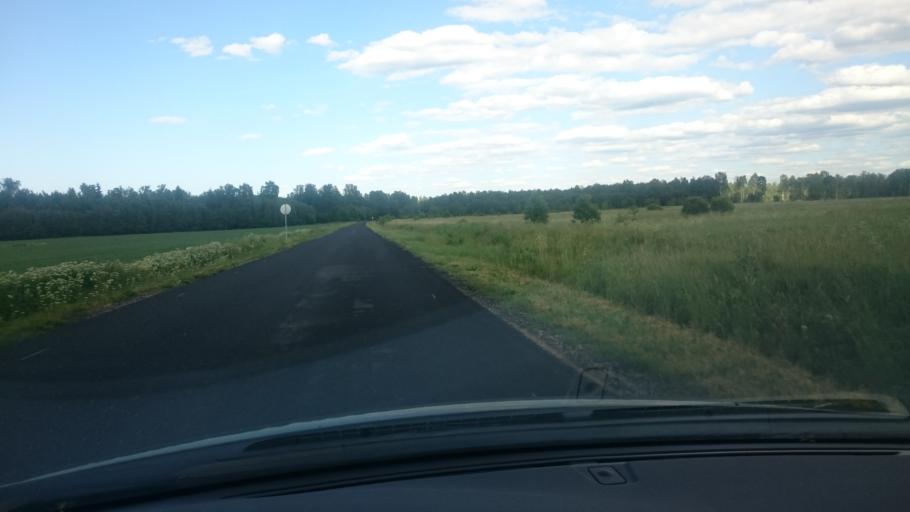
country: EE
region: Harju
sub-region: Rae vald
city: Vaida
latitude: 59.2281
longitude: 24.9747
